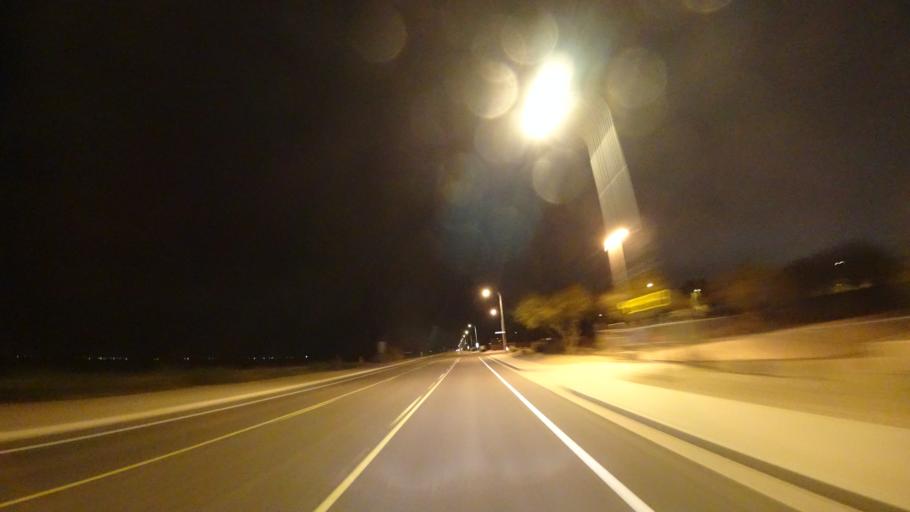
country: US
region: Arizona
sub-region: Maricopa County
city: Sun Lakes
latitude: 33.2047
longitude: -111.8054
